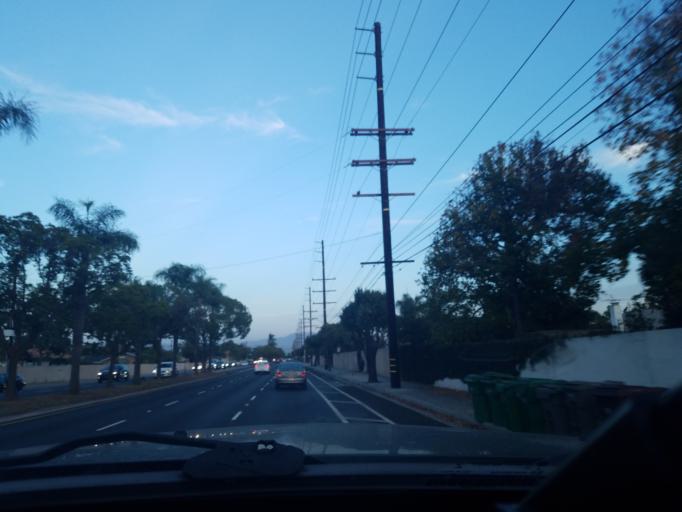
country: US
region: California
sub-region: Orange County
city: Santa Ana
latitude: 33.7153
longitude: -117.9030
